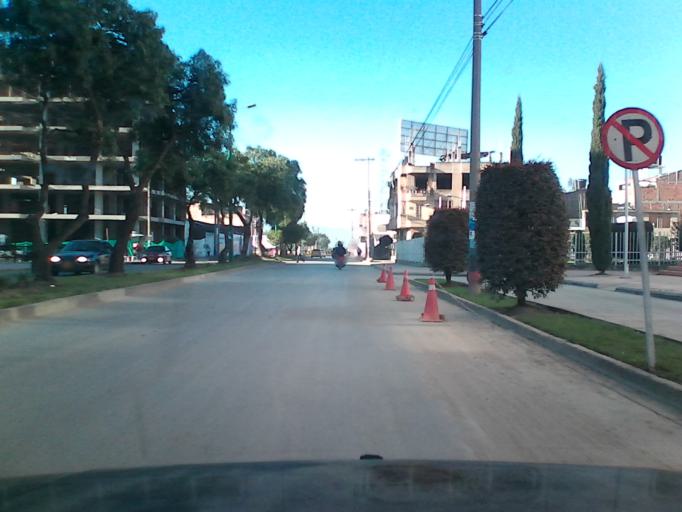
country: CO
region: Boyaca
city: Duitama
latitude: 5.8147
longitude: -73.0307
